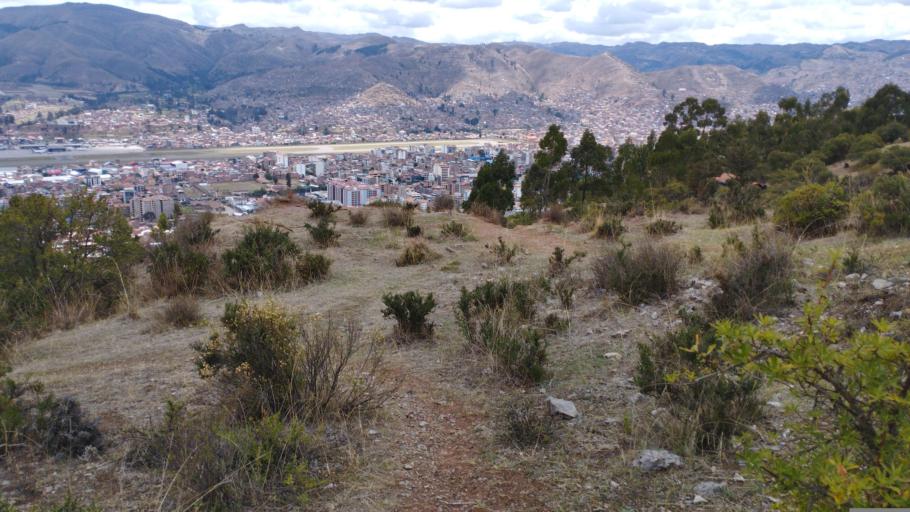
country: PE
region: Cusco
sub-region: Provincia de Cusco
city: Cusco
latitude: -13.5184
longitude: -71.9398
